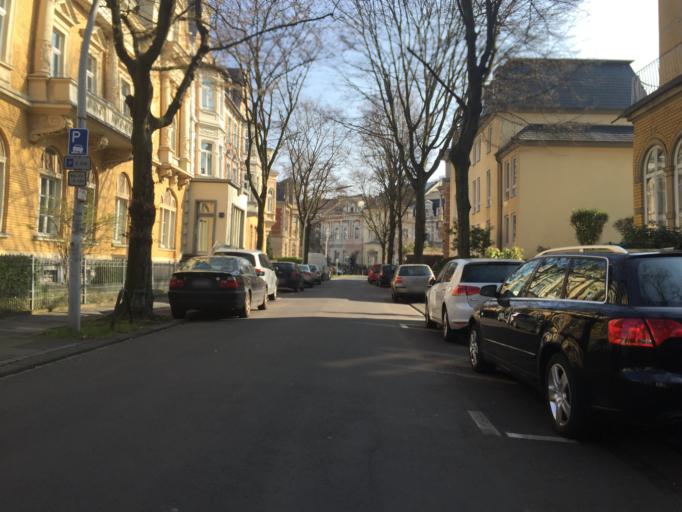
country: DE
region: North Rhine-Westphalia
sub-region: Regierungsbezirk Koln
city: Bonn
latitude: 50.7329
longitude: 7.0898
